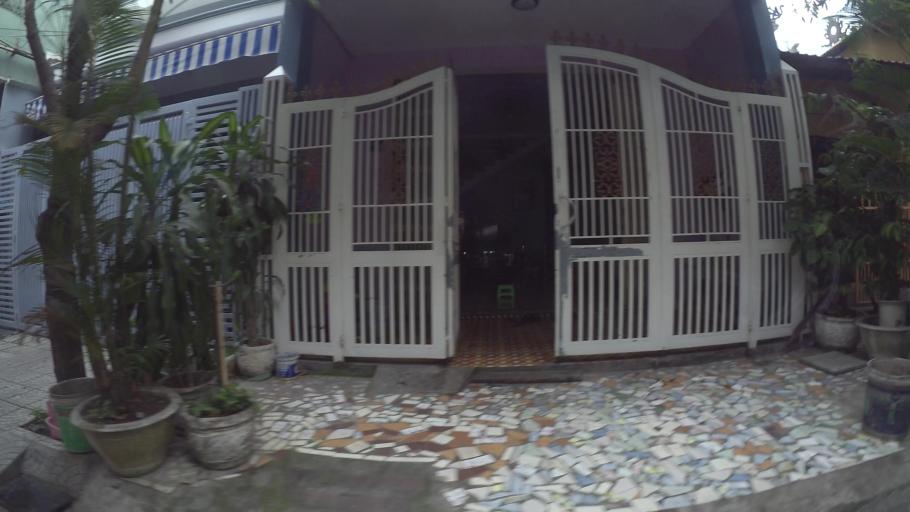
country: VN
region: Da Nang
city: Thanh Khe
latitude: 16.0714
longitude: 108.1865
